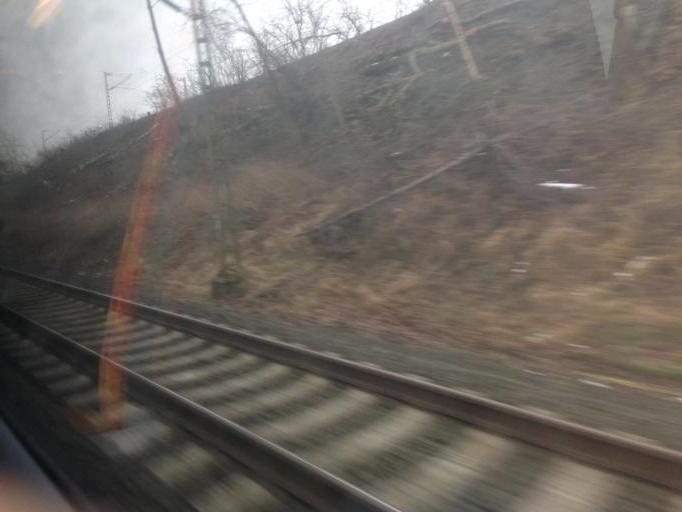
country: DE
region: Hesse
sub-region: Regierungsbezirk Giessen
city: Heuchelheim
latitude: 50.5646
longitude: 8.6421
